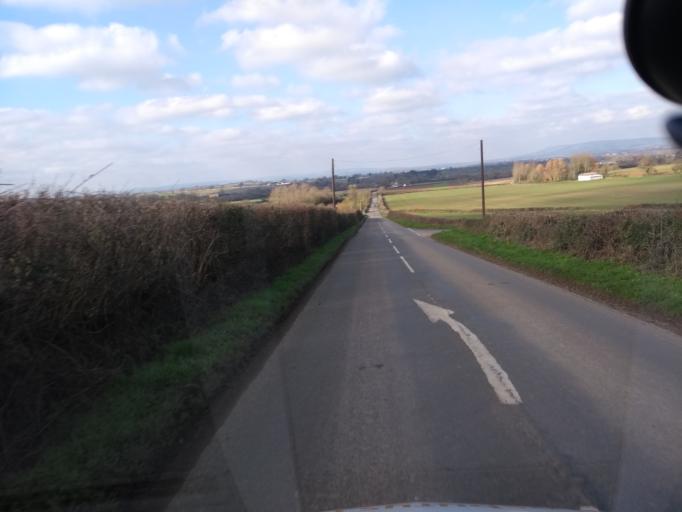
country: GB
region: England
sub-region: Somerset
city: Creech Saint Michael
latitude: 50.9814
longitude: -3.0568
